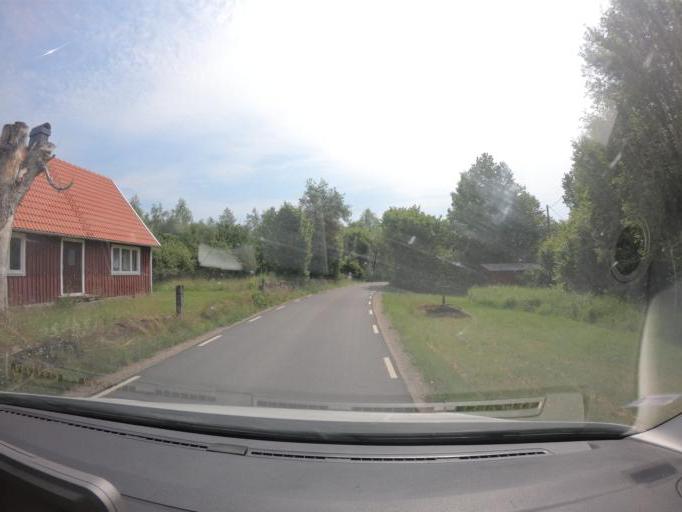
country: SE
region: Skane
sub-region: Hassleholms Kommun
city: Bjarnum
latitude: 56.2530
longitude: 13.6864
